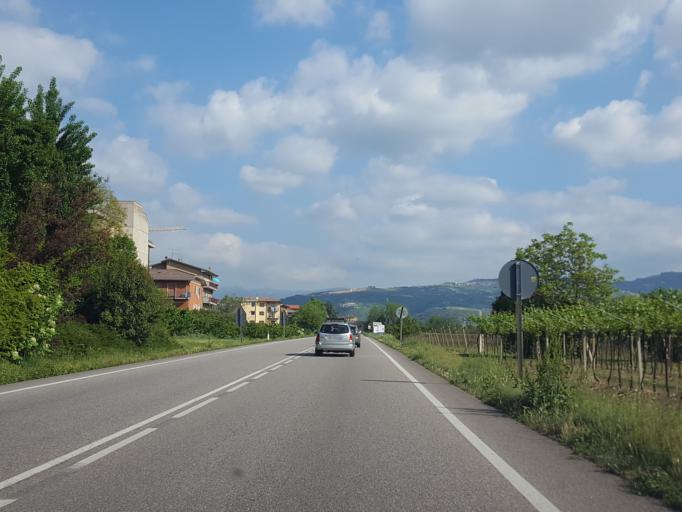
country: IT
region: Veneto
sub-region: Provincia di Verona
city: Poiano
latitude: 45.4924
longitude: 11.0215
